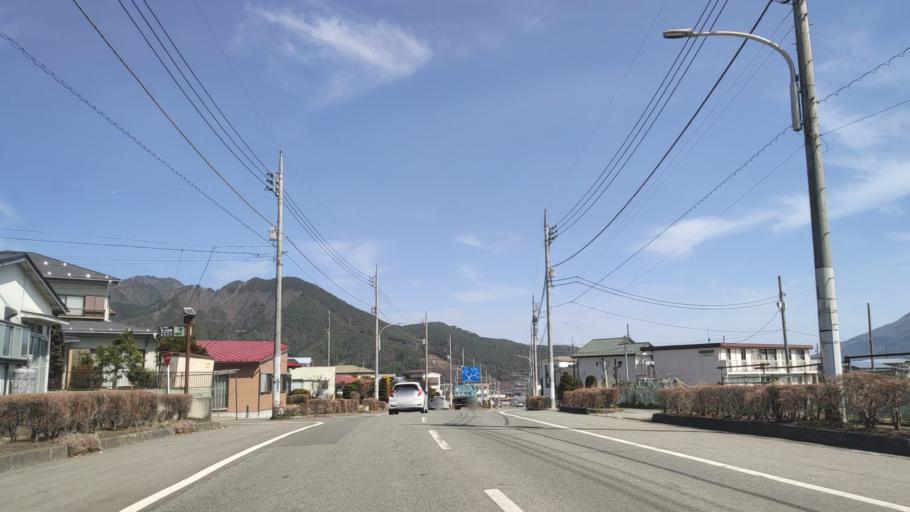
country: JP
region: Yamanashi
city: Fujikawaguchiko
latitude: 35.4882
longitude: 138.7902
